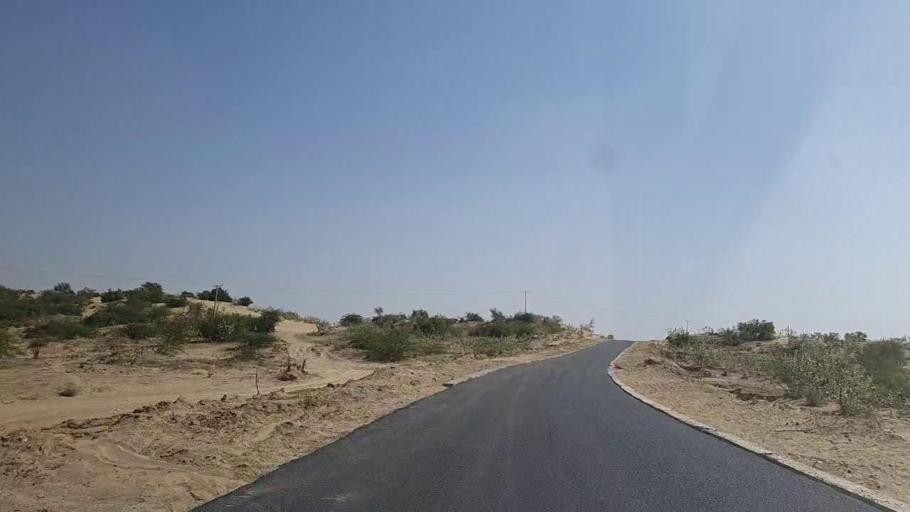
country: PK
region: Sindh
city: Diplo
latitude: 24.4803
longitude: 69.5276
